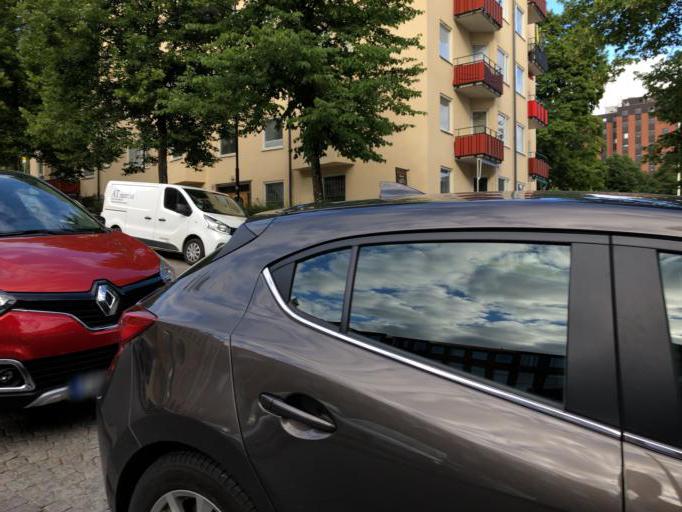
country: SE
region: Stockholm
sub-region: Sundbybergs Kommun
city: Sundbyberg
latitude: 59.3622
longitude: 17.9733
